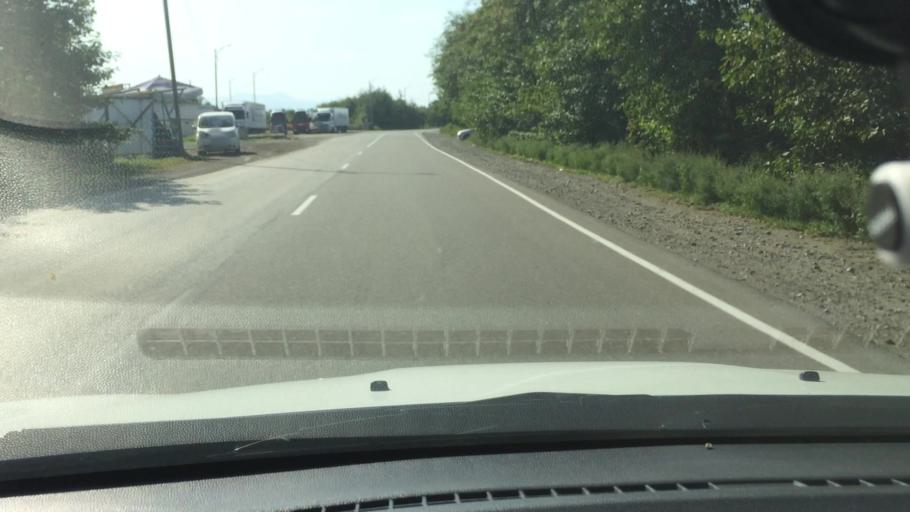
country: GE
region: Guria
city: Urek'i
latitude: 41.9607
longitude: 41.7729
